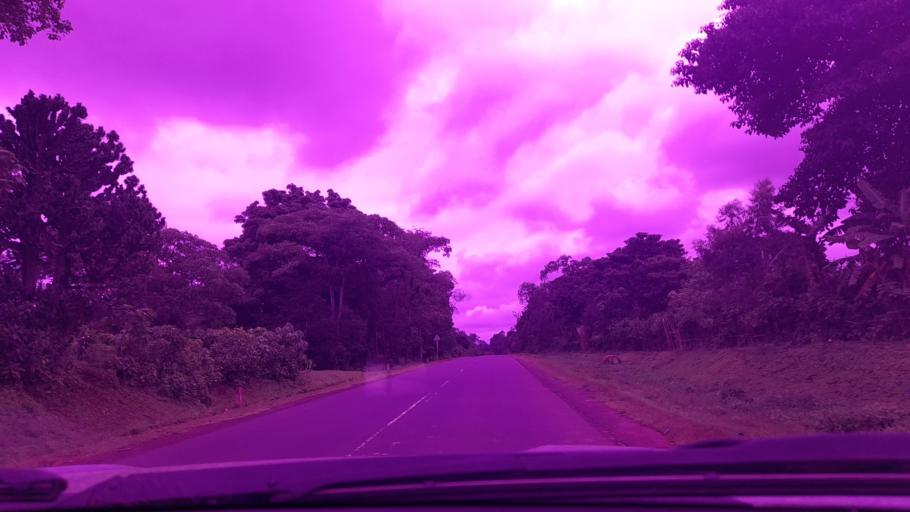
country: ET
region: Southern Nations, Nationalities, and People's Region
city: Bonga
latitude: 7.2796
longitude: 35.9516
